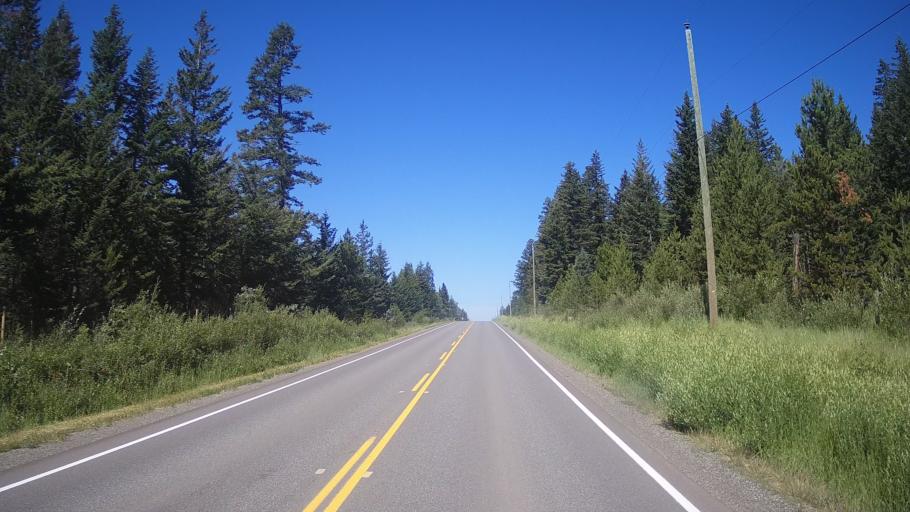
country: CA
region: British Columbia
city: Cache Creek
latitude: 51.5416
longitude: -121.0549
